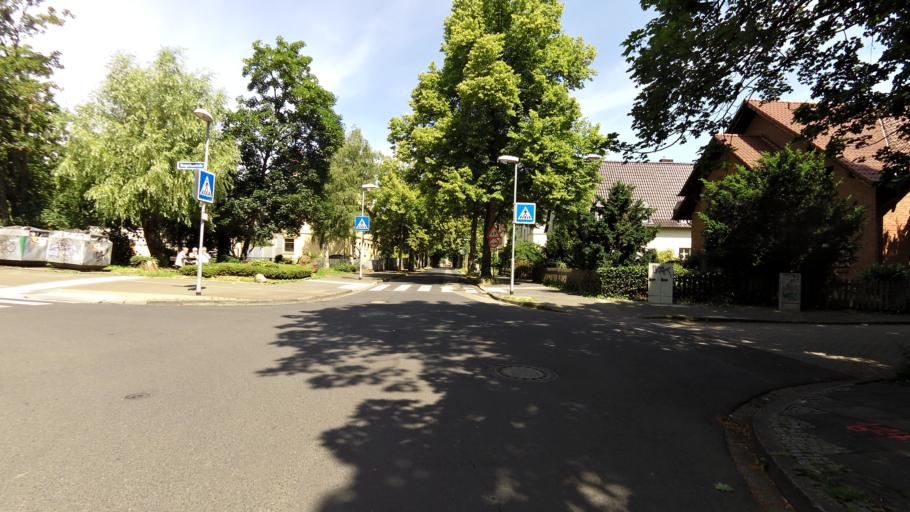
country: DE
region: North Rhine-Westphalia
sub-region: Regierungsbezirk Koln
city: Rheinbach
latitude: 50.6220
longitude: 6.9509
